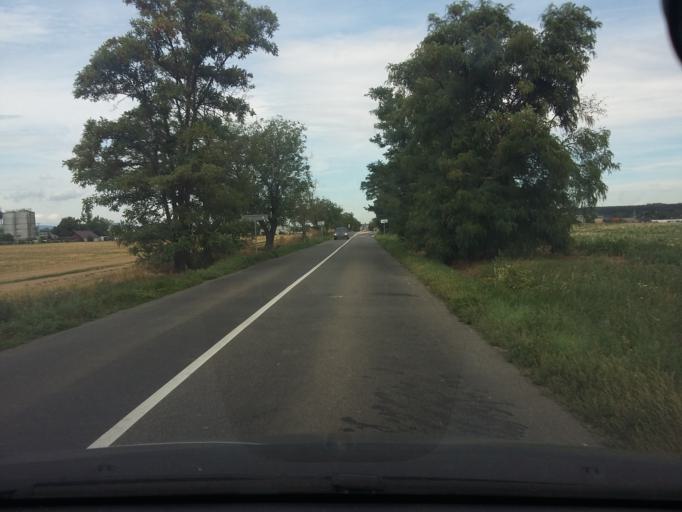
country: SK
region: Bratislavsky
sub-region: Okres Pezinok
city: Pezinok
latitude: 48.2616
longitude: 17.2981
